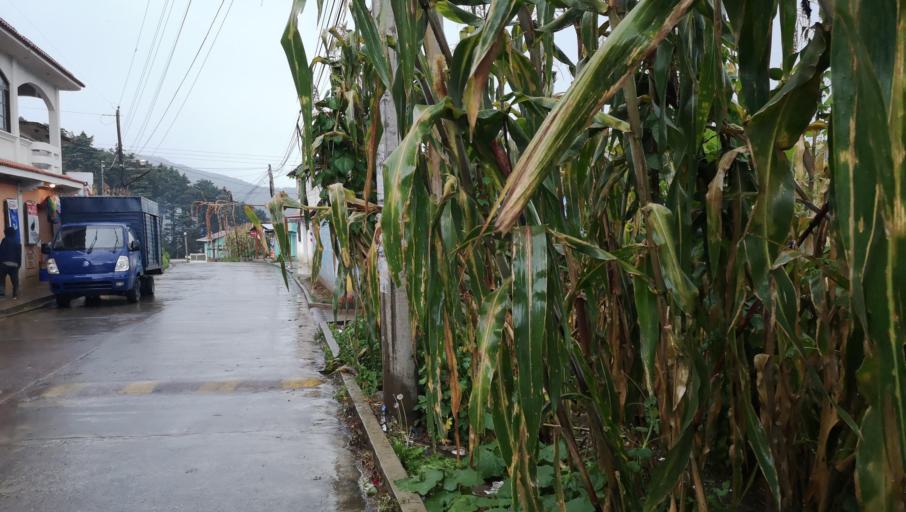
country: GT
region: Quetzaltenango
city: Cantel
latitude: 14.8185
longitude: -91.4486
